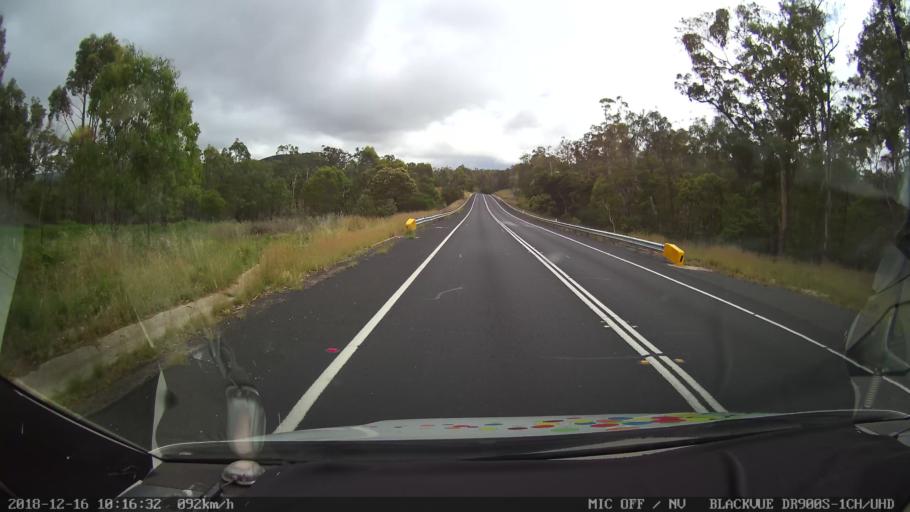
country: AU
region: New South Wales
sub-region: Tenterfield Municipality
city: Carrolls Creek
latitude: -29.2658
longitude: 151.9837
